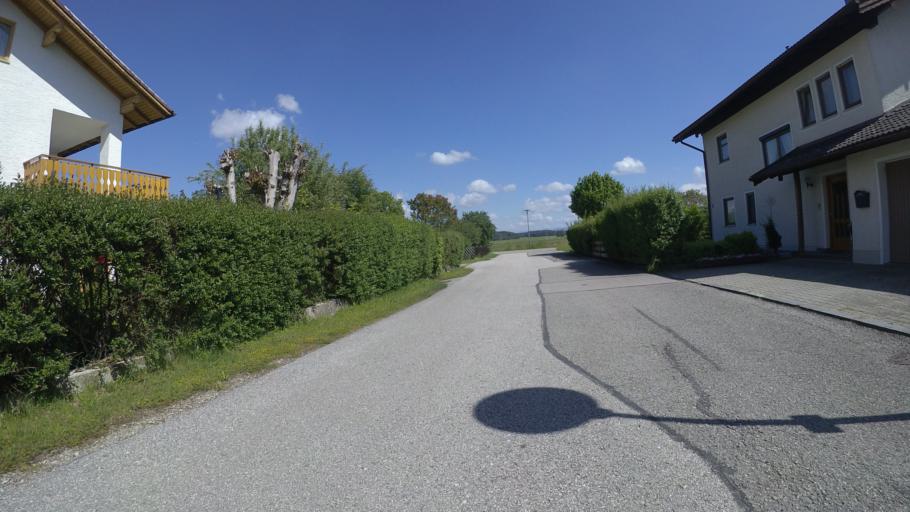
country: DE
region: Bavaria
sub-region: Upper Bavaria
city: Traunreut
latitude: 47.9393
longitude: 12.6081
